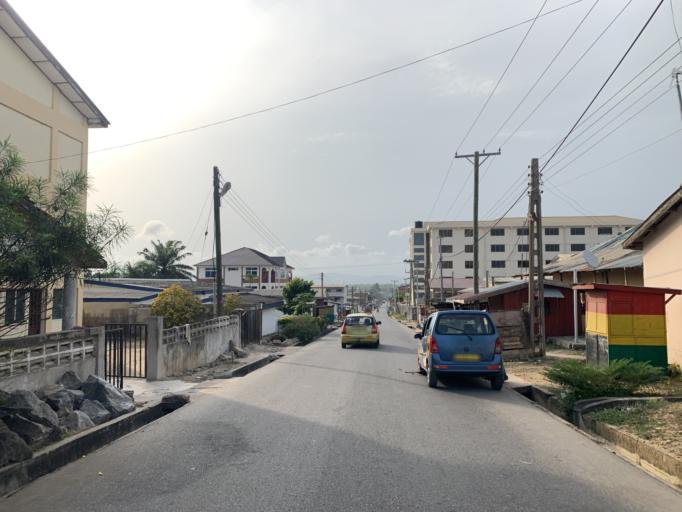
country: GH
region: Central
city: Winneba
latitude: 5.3444
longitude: -0.6252
